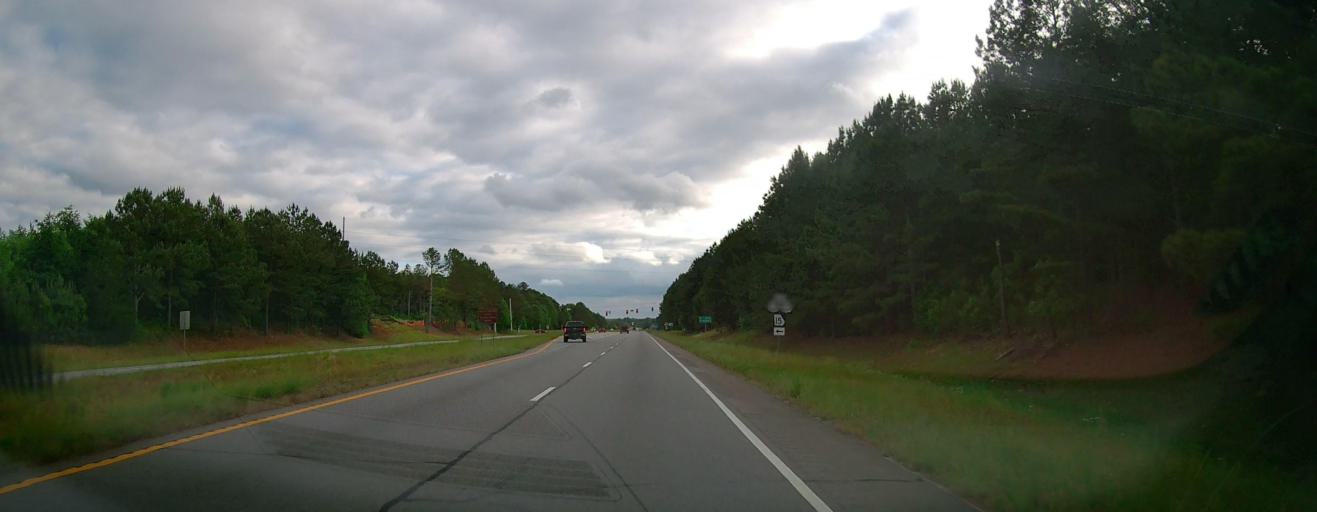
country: US
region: Georgia
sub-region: Oconee County
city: Watkinsville
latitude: 33.8831
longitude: -83.4138
